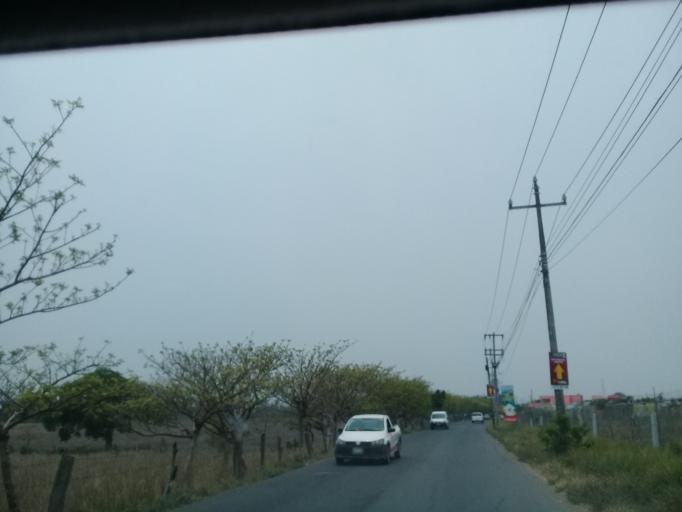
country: MX
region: Veracruz
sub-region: Veracruz
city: Las Amapolas
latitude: 19.1506
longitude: -96.2128
